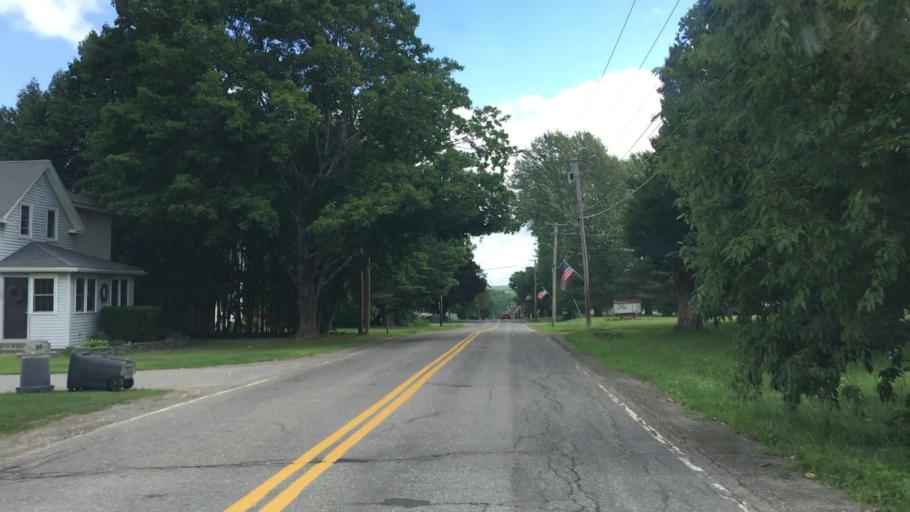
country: US
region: Maine
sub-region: Penobscot County
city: Carmel
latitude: 44.7961
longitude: -69.0569
